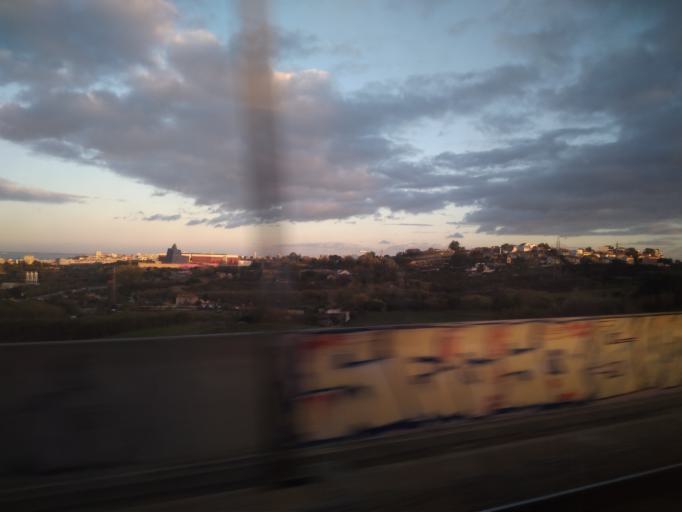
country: PT
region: Setubal
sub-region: Almada
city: Sobreda
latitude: 38.6593
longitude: -9.1859
